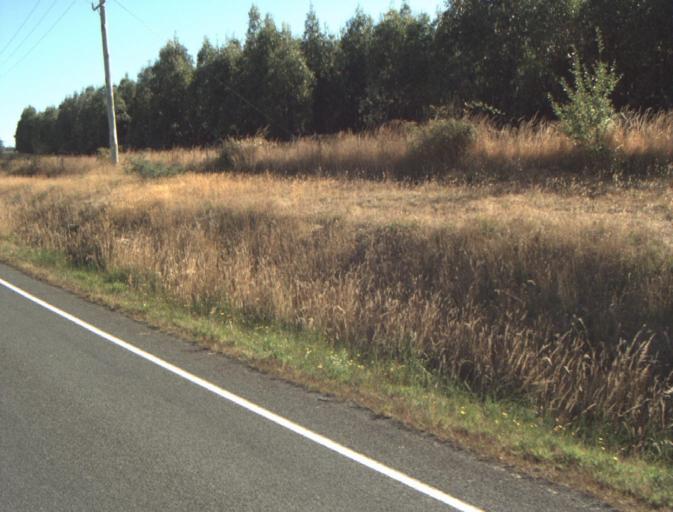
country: AU
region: Tasmania
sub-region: Launceston
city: Newstead
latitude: -41.4144
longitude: 147.2804
